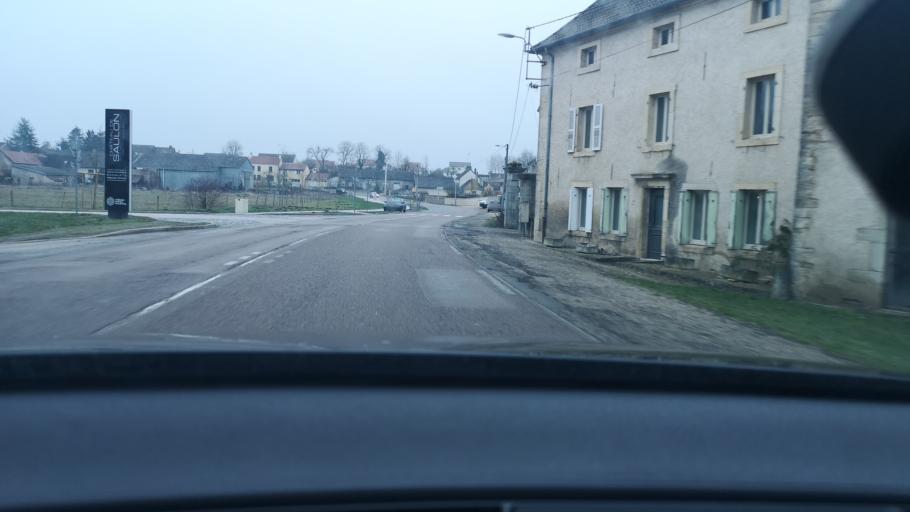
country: FR
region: Bourgogne
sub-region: Departement de la Cote-d'Or
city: Fenay
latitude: 47.2253
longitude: 5.0628
